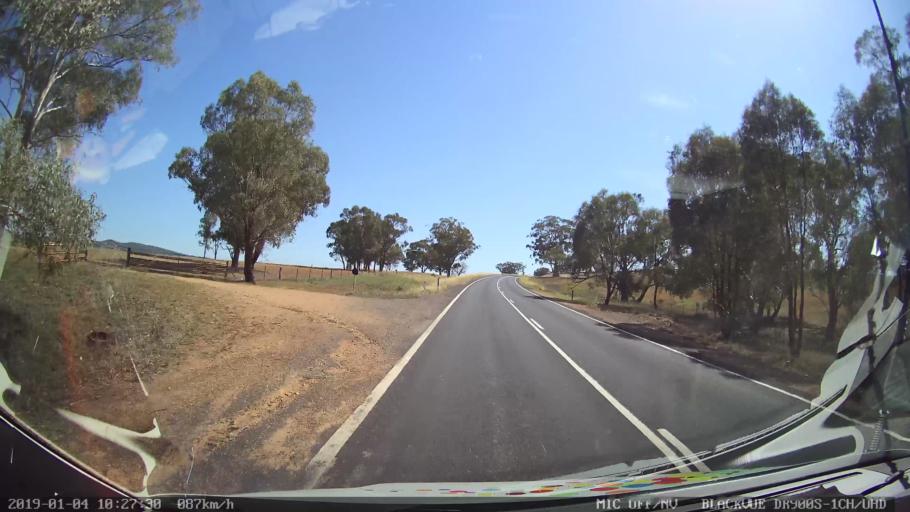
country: AU
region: New South Wales
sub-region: Cabonne
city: Canowindra
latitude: -33.3695
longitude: 148.5988
